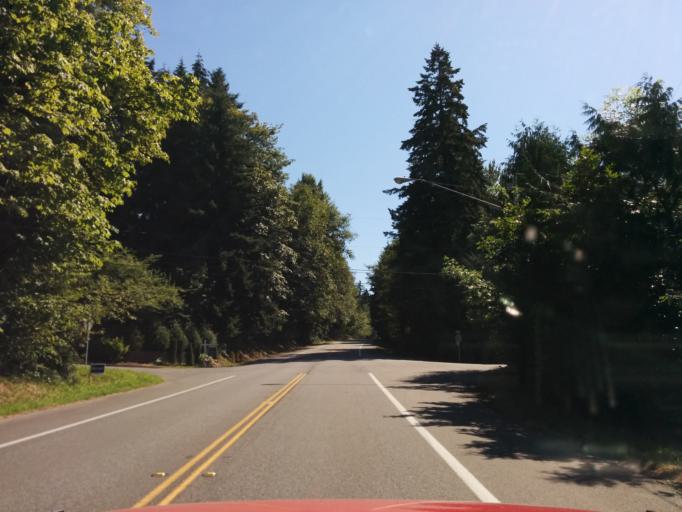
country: US
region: Washington
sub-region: King County
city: West Lake Sammamish
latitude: 47.5962
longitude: -122.0818
